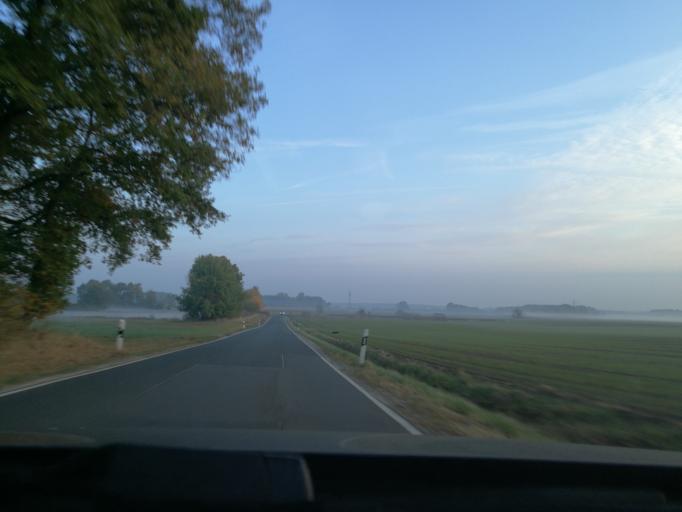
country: DE
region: Bavaria
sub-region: Regierungsbezirk Mittelfranken
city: Obermichelbach
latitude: 49.5455
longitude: 10.9119
